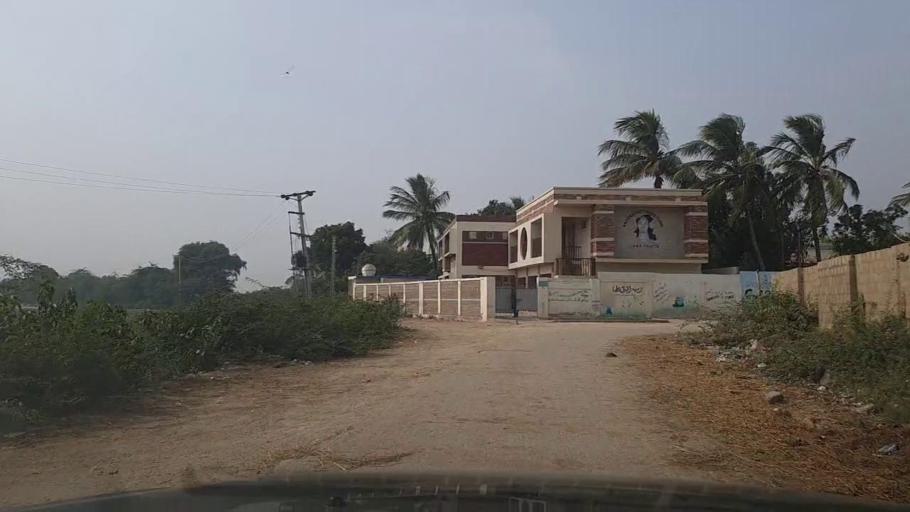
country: PK
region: Sindh
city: Mirpur Sakro
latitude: 24.5511
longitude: 67.8396
